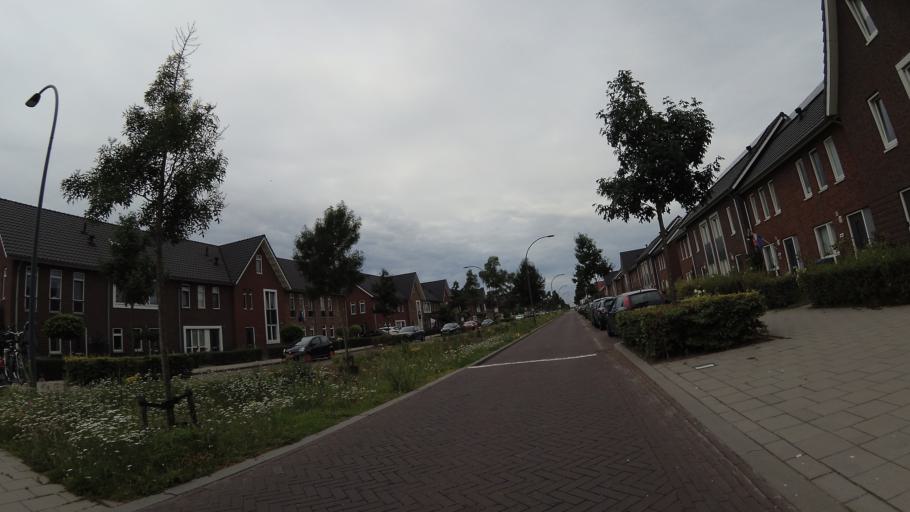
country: NL
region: North Brabant
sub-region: Gemeente Oosterhout
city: Oosterhout
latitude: 51.6493
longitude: 4.8297
